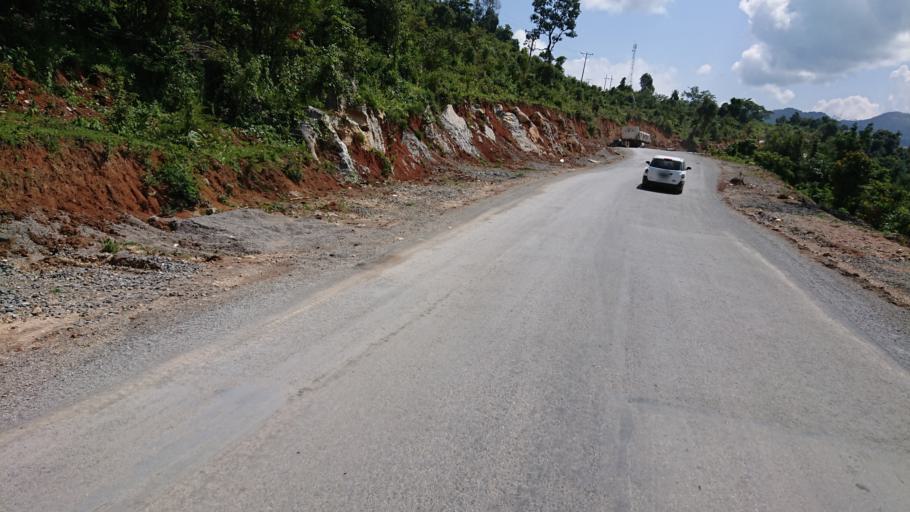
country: MM
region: Shan
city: Taunggyi
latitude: 20.8131
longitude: 97.3184
